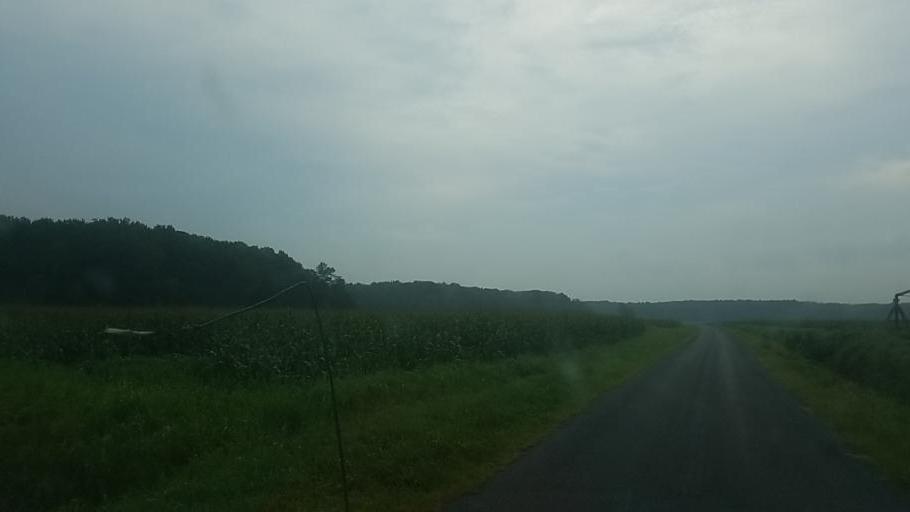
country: US
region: Delaware
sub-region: Sussex County
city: Selbyville
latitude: 38.4487
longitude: -75.2831
